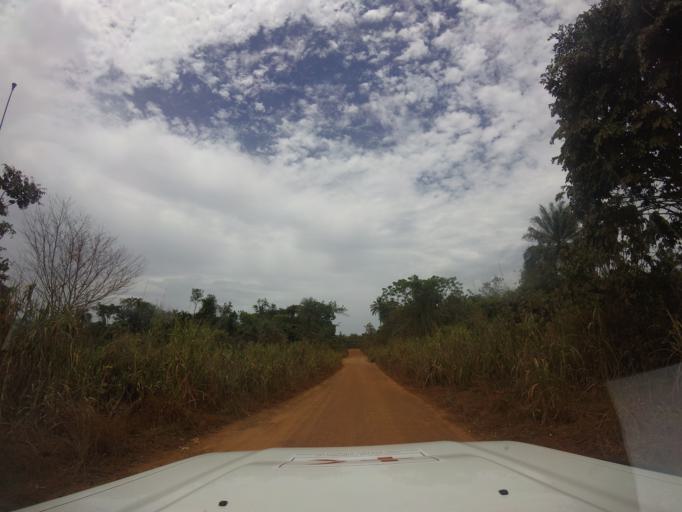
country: LR
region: Grand Cape Mount
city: Robertsport
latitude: 7.0135
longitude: -11.2888
